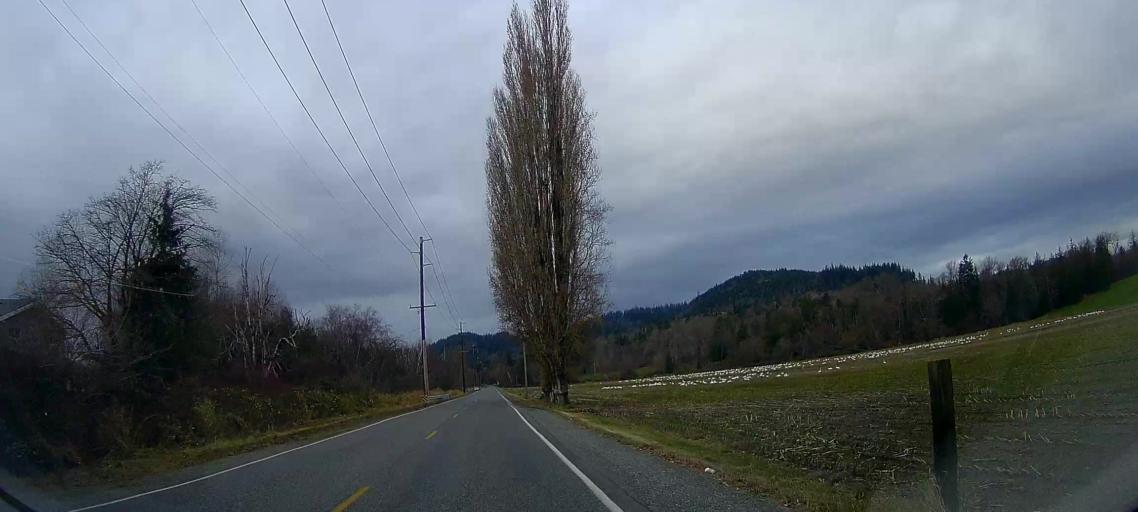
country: US
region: Washington
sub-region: Skagit County
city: Sedro-Woolley
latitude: 48.5250
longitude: -122.2739
